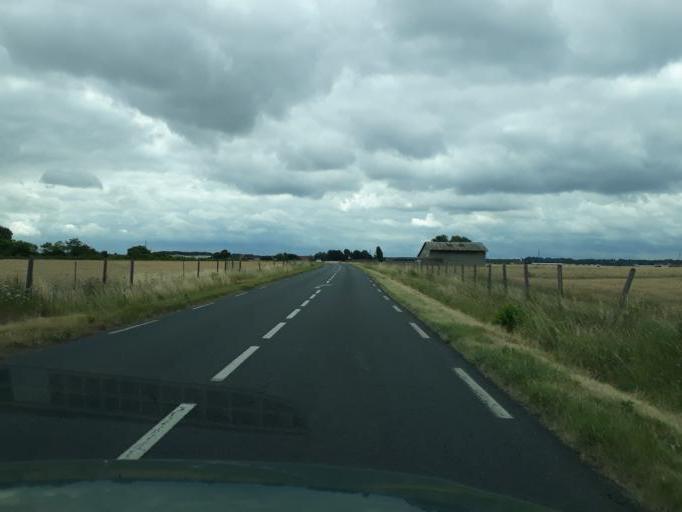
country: FR
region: Centre
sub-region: Departement du Loiret
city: Saint-Denis-en-Val
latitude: 47.8665
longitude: 1.9441
